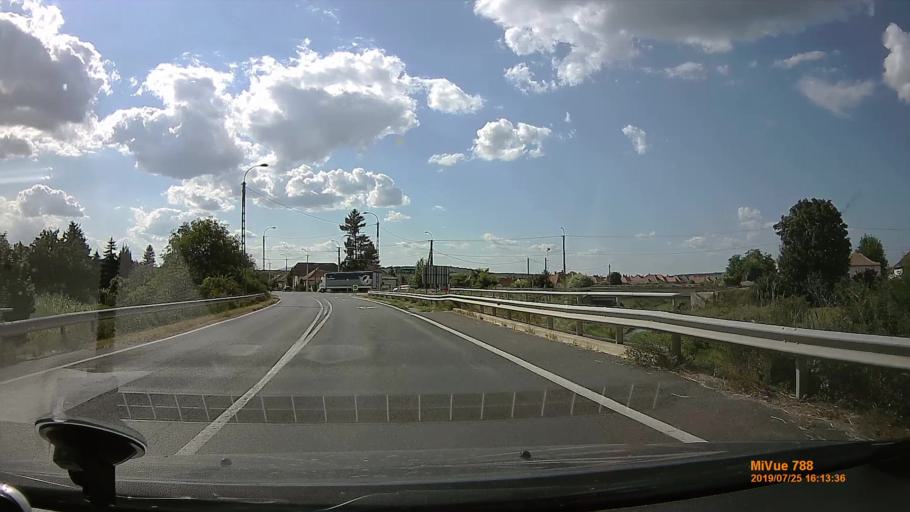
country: HU
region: Heves
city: Kerecsend
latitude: 47.7933
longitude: 20.3383
